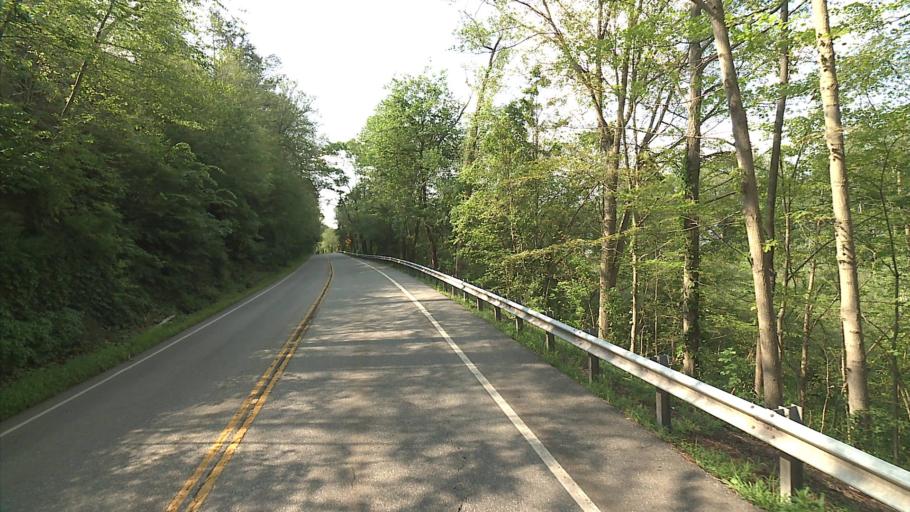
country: US
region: Connecticut
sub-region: Middlesex County
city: East Haddam
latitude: 41.4667
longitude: -72.4654
